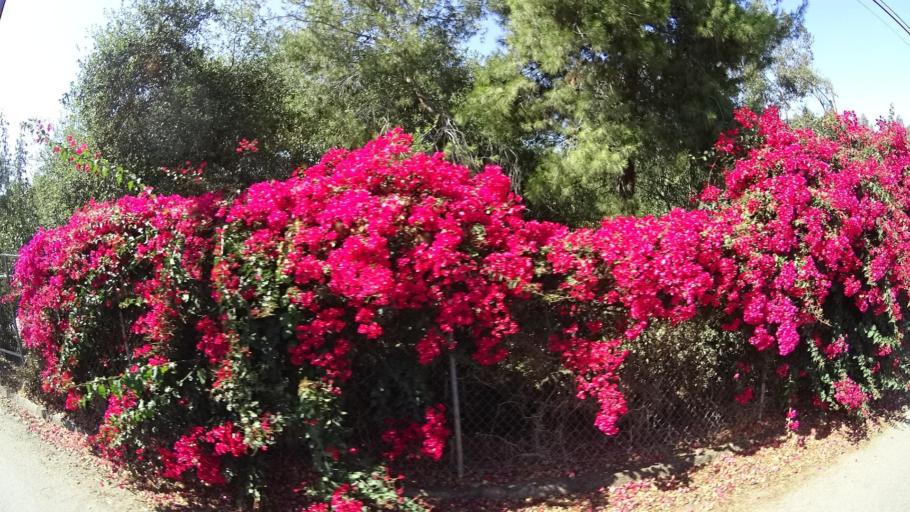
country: US
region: California
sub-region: San Diego County
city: Crest
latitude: 32.8037
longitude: -116.8693
